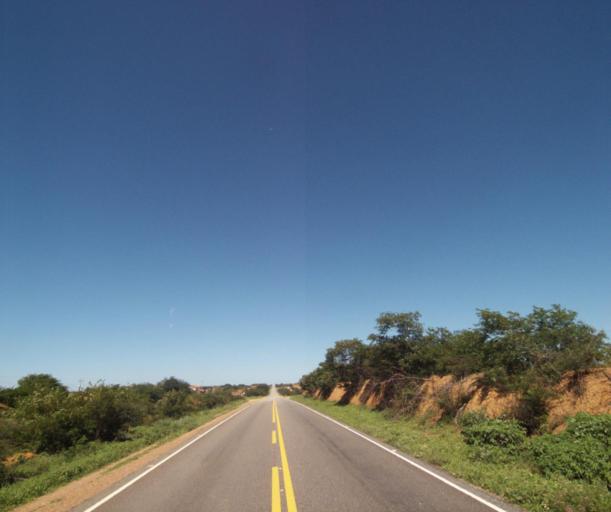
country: BR
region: Bahia
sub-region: Palmas De Monte Alto
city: Palmas de Monte Alto
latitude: -14.2546
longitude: -43.2261
